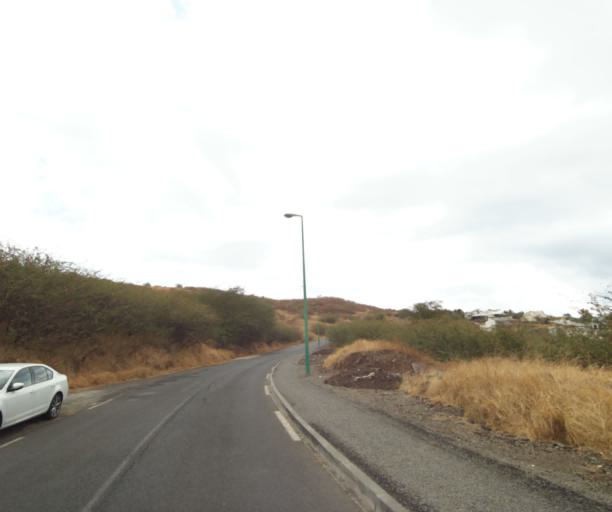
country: RE
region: Reunion
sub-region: Reunion
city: Saint-Paul
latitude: -21.0591
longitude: 55.2330
